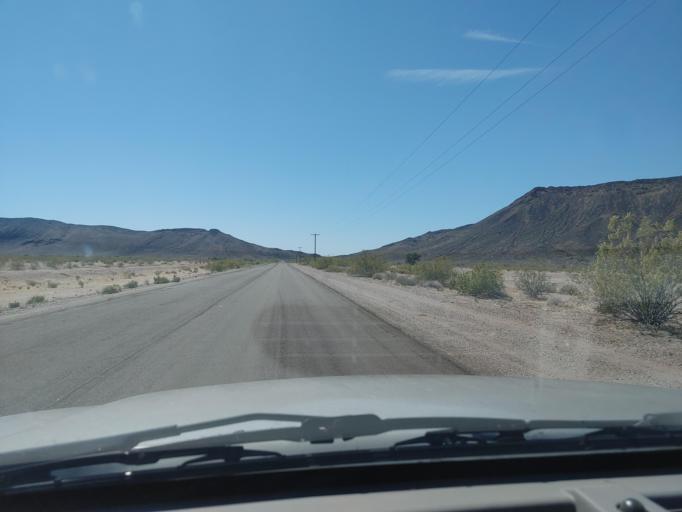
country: US
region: Arizona
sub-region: Maricopa County
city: Gila Bend
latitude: 33.0181
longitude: -113.3404
